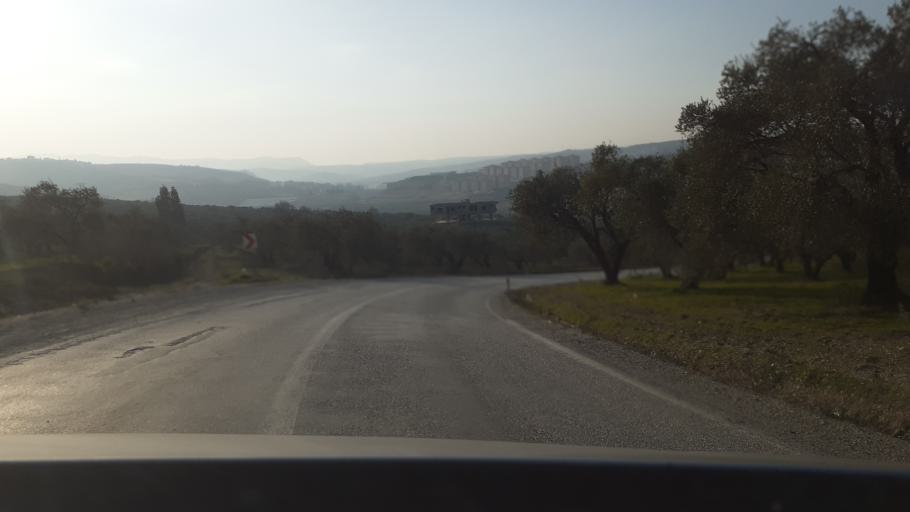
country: TR
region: Hatay
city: Oymakli
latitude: 36.1134
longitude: 36.2870
